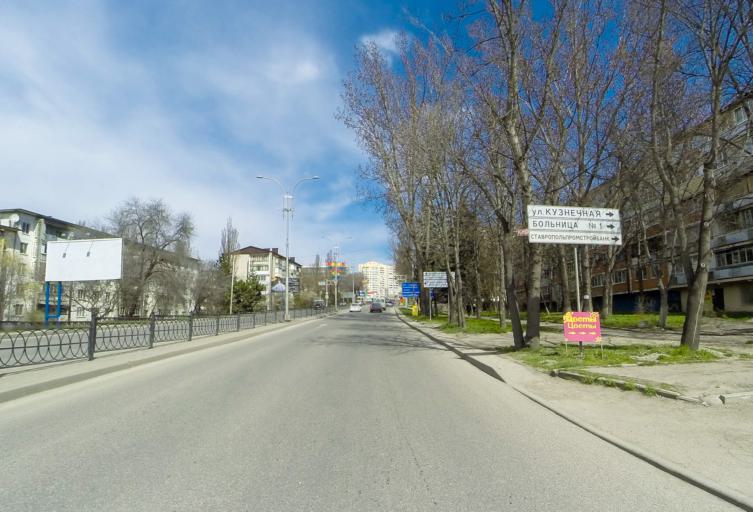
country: RU
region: Stavropol'skiy
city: Pyatigorsk
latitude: 44.0502
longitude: 43.0651
